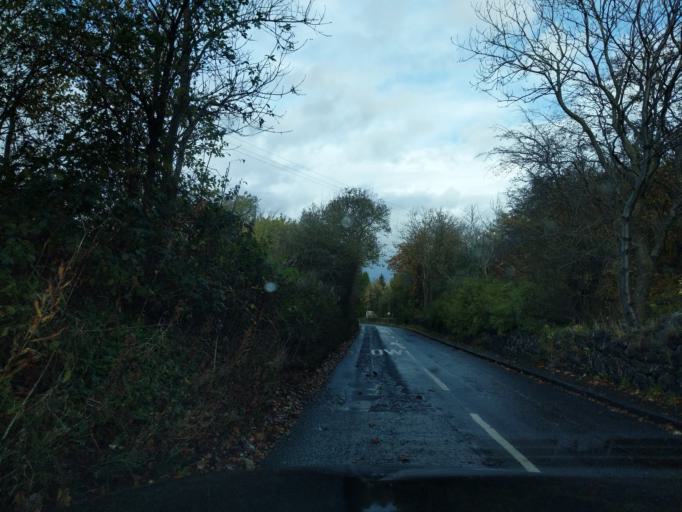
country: GB
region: Scotland
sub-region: Edinburgh
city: Newbridge
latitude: 55.9318
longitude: -3.3895
